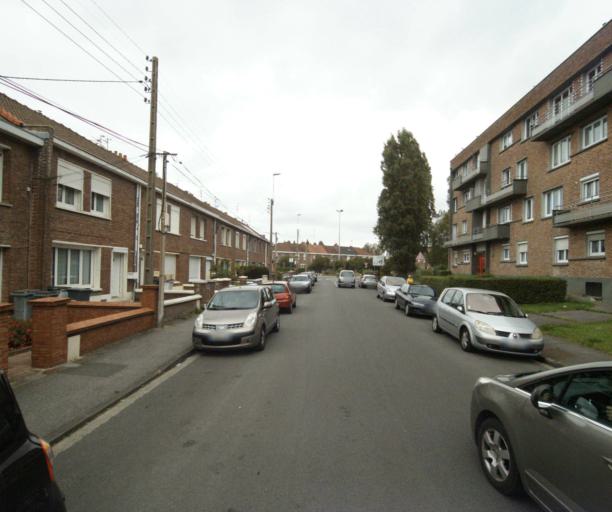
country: FR
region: Nord-Pas-de-Calais
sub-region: Departement du Nord
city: Ronchin
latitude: 50.6022
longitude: 3.0822
